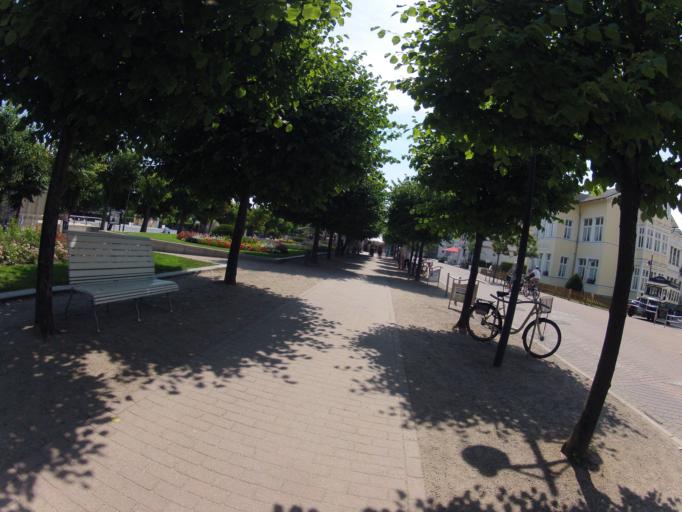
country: DE
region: Mecklenburg-Vorpommern
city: Seebad Heringsdorf
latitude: 53.9427
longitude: 14.1890
